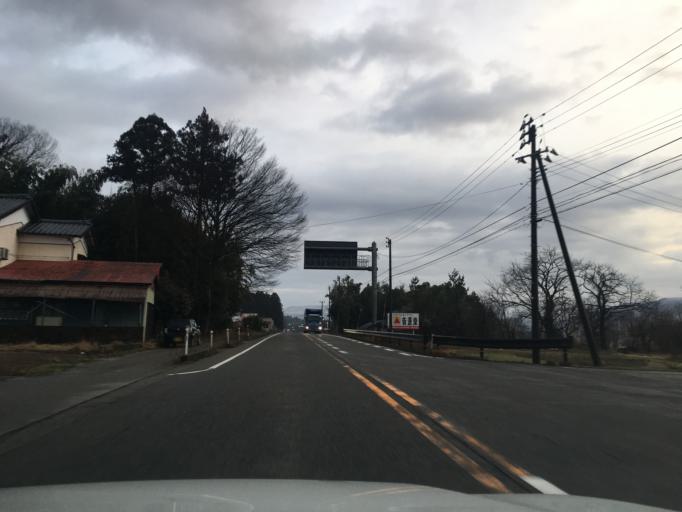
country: JP
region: Niigata
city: Murakami
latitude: 38.2845
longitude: 139.5230
